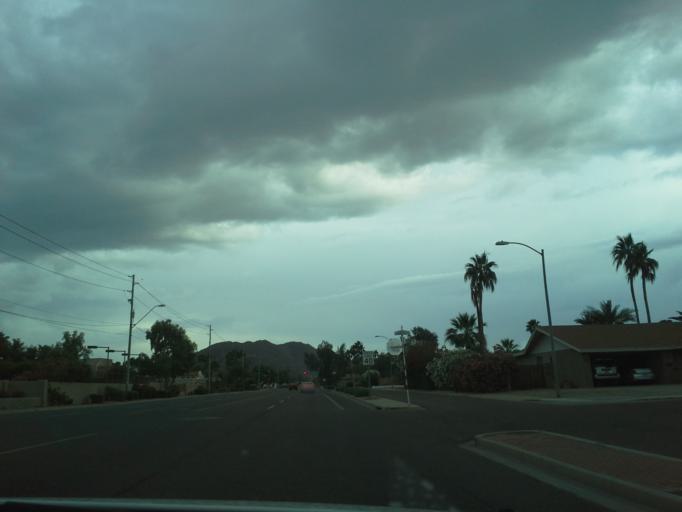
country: US
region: Arizona
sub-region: Maricopa County
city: Paradise Valley
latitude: 33.5926
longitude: -111.9959
